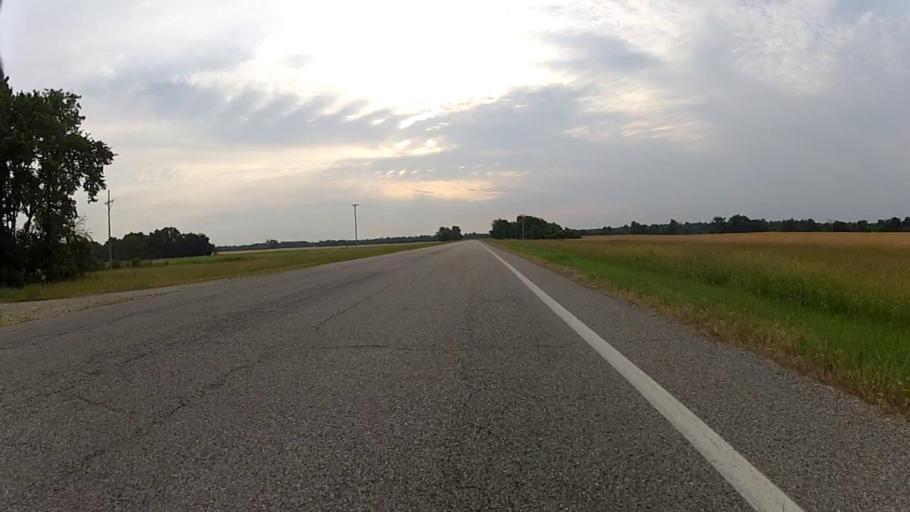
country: US
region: Kansas
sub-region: Labette County
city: Oswego
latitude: 37.1788
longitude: -94.9888
